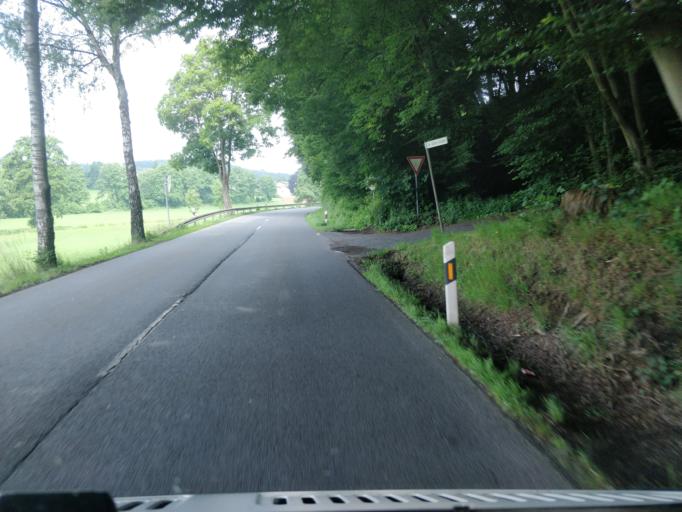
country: DE
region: North Rhine-Westphalia
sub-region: Regierungsbezirk Koln
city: Numbrecht
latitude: 50.9089
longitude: 7.5892
